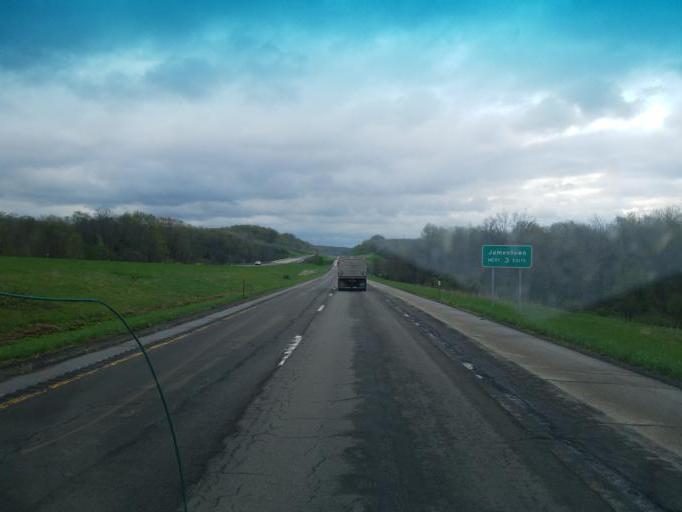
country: US
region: New York
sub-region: Chautauqua County
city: Lakewood
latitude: 42.1280
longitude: -79.3151
